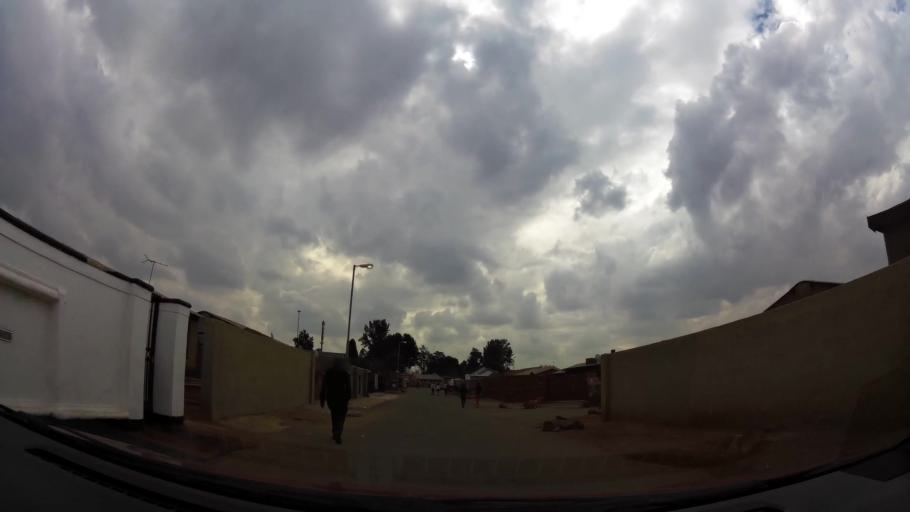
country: ZA
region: Gauteng
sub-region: City of Johannesburg Metropolitan Municipality
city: Soweto
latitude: -26.2641
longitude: 27.8356
